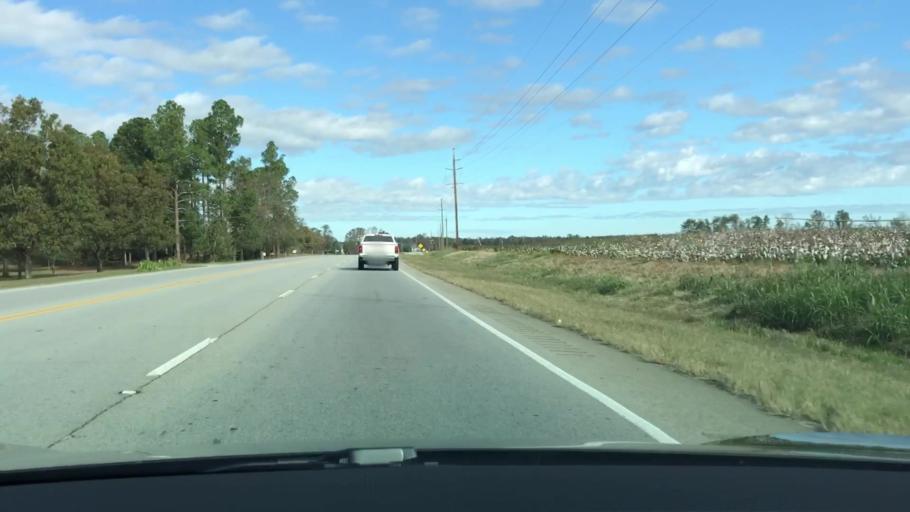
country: US
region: Georgia
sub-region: Jefferson County
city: Louisville
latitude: 33.0372
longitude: -82.4059
